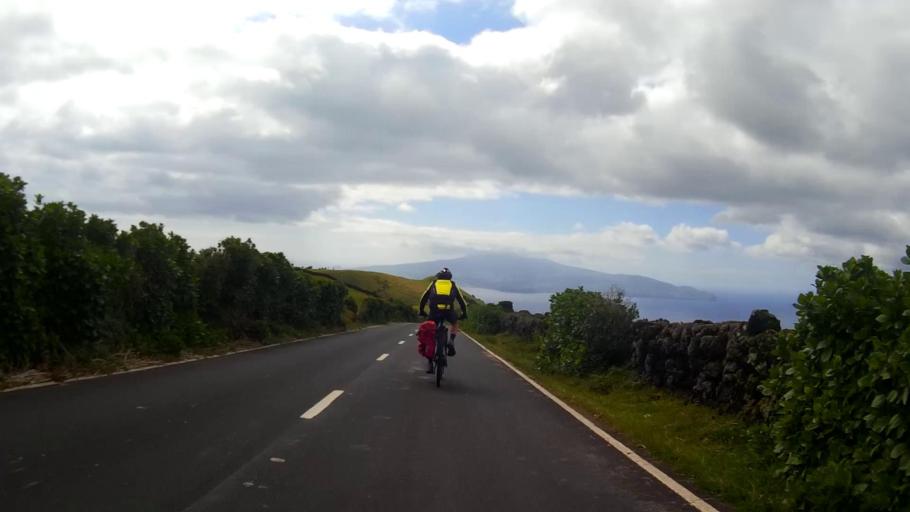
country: PT
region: Azores
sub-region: Madalena
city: Madalena
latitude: 38.4959
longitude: -28.4571
